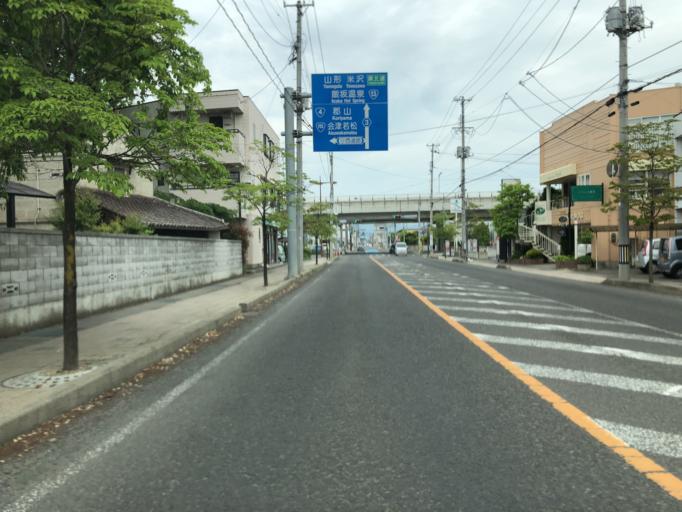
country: JP
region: Fukushima
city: Fukushima-shi
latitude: 37.7762
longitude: 140.4472
